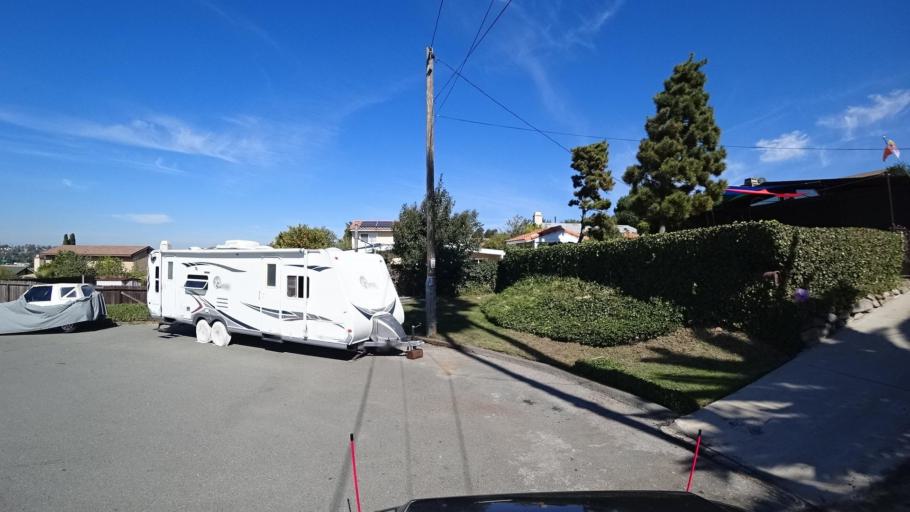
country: US
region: California
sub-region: San Diego County
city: La Presa
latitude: 32.7037
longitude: -117.0050
